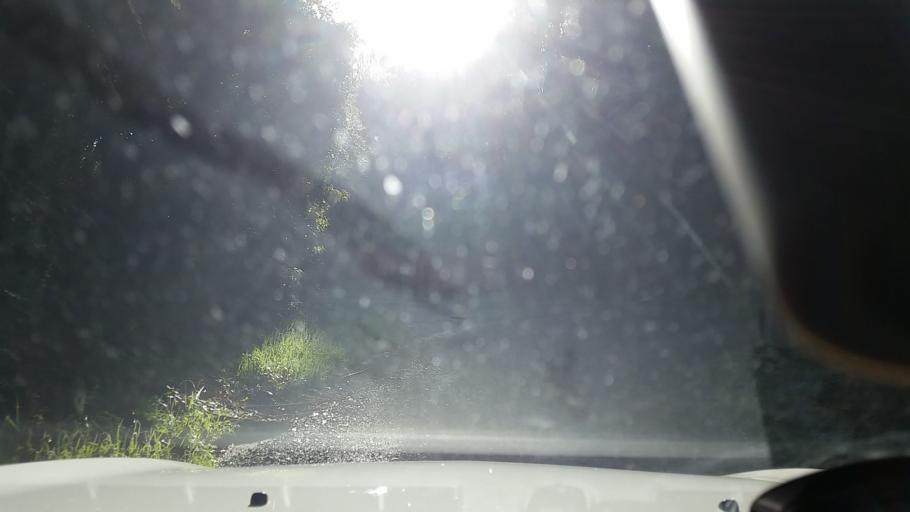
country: NZ
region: Bay of Plenty
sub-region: Kawerau District
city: Kawerau
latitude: -38.0220
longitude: 176.5690
